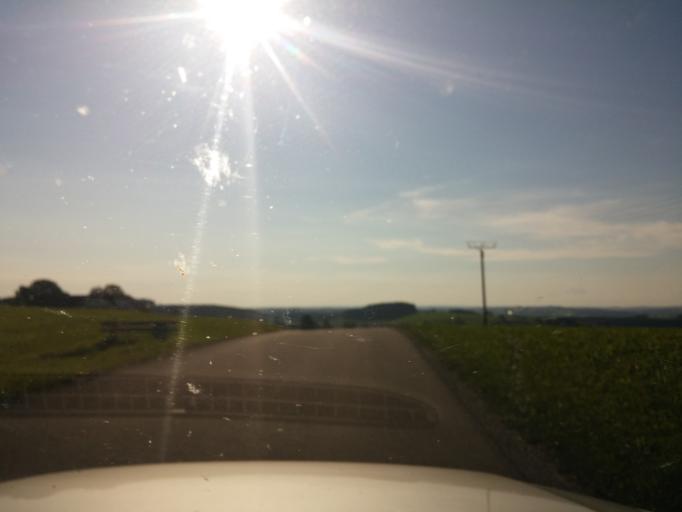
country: DE
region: Bavaria
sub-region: Swabia
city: Legau
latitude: 47.7804
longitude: 10.1078
